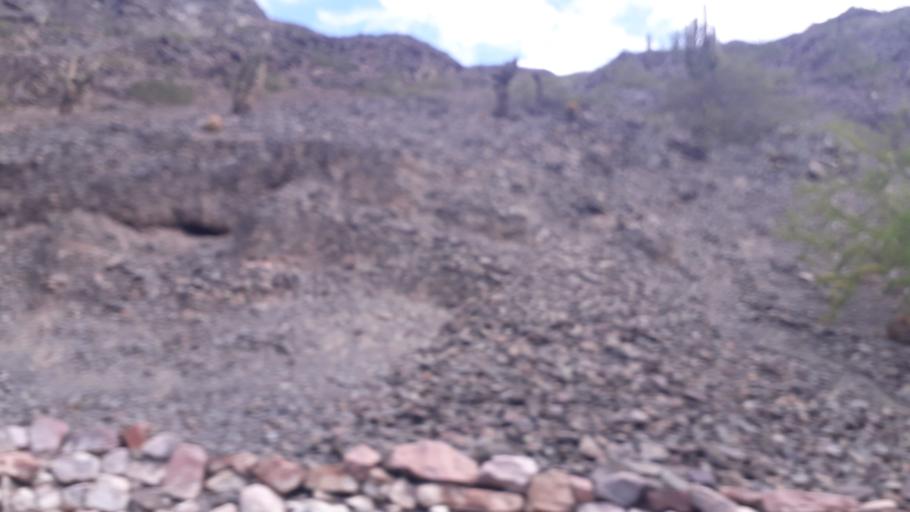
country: AR
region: Jujuy
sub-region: Departamento de Tumbaya
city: Tumbaya
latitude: -23.7461
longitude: -65.4784
